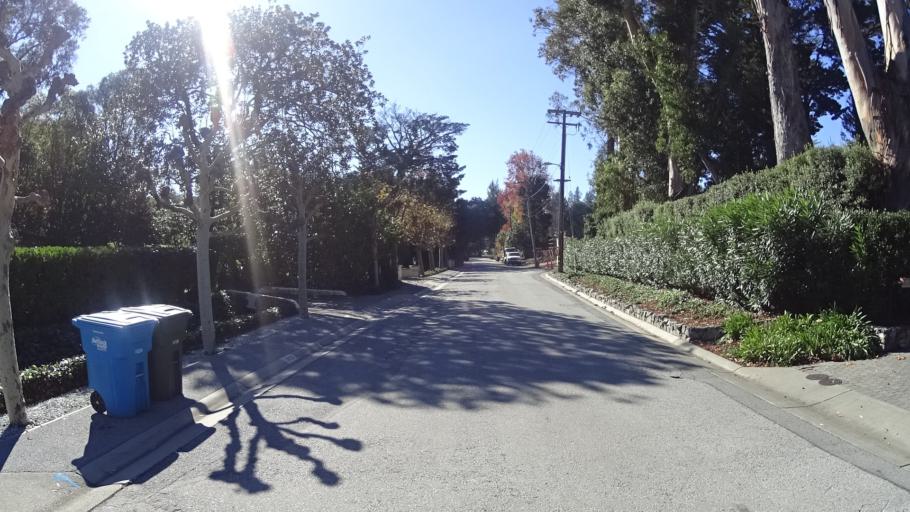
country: US
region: California
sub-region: San Mateo County
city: Burlingame
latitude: 37.5754
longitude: -122.3635
